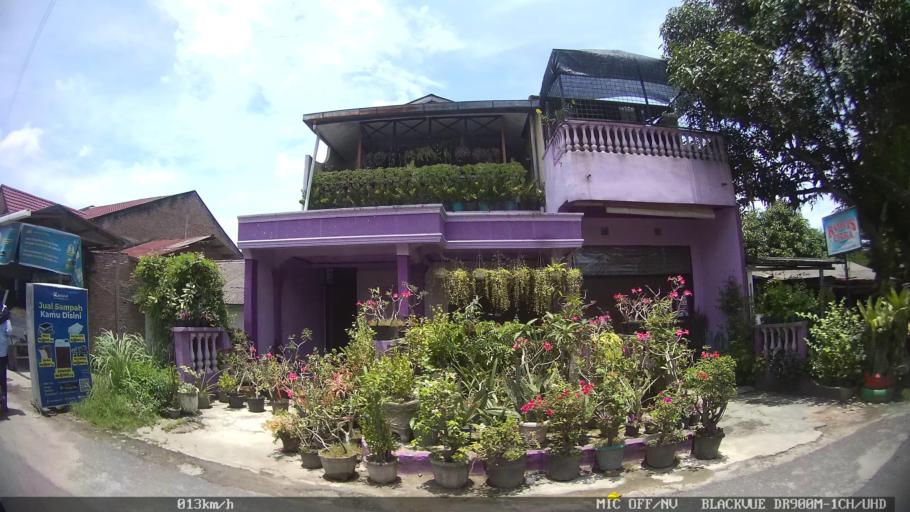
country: ID
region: North Sumatra
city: Percut
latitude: 3.5427
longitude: 98.8759
